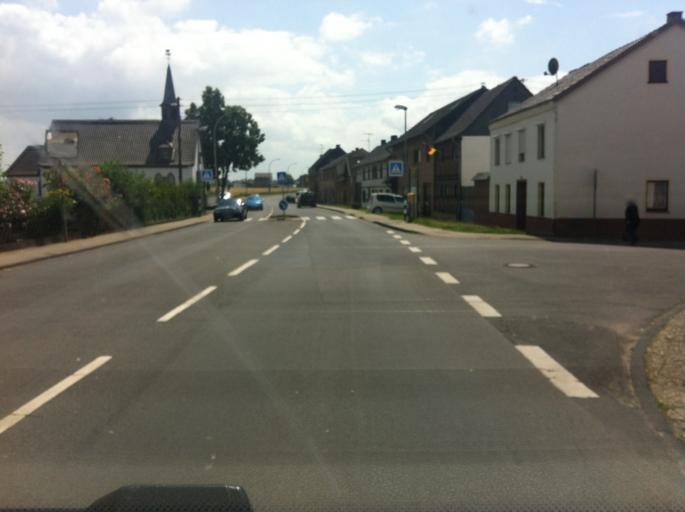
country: DE
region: North Rhine-Westphalia
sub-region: Regierungsbezirk Koln
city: Weilerswist
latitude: 50.7167
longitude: 6.8166
